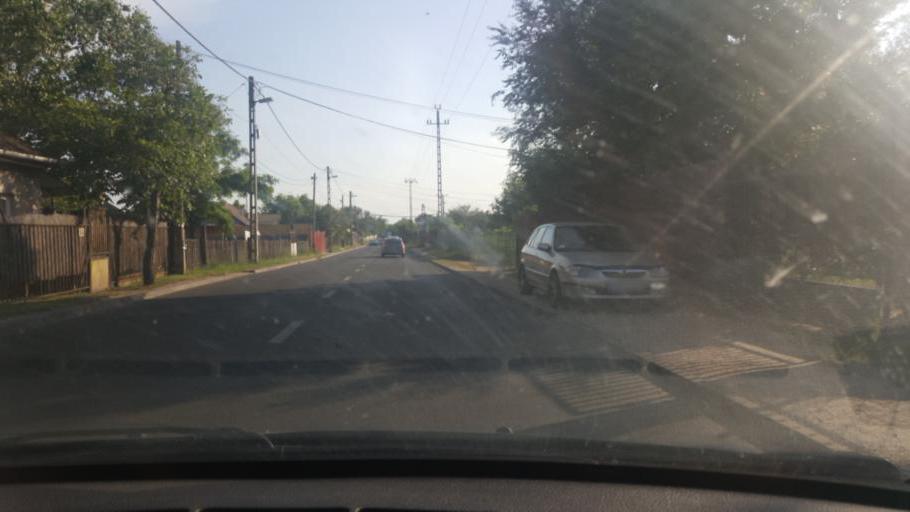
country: HU
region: Budapest
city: Budapest XVII. keruelet
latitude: 47.4558
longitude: 19.2233
